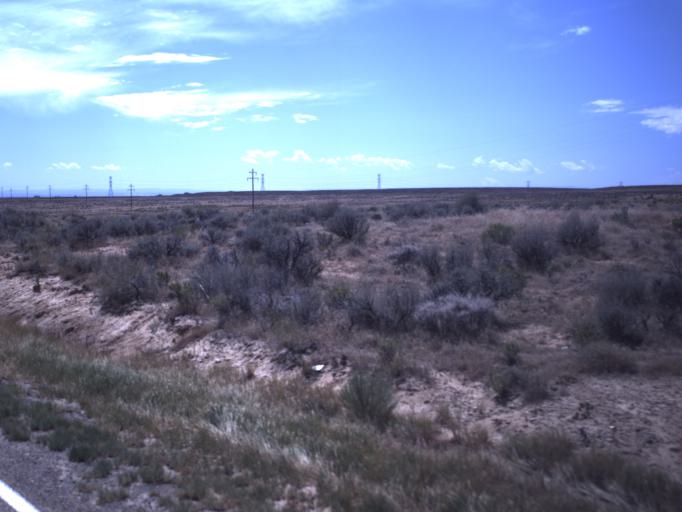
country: US
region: Utah
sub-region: Uintah County
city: Maeser
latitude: 40.2902
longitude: -109.6851
